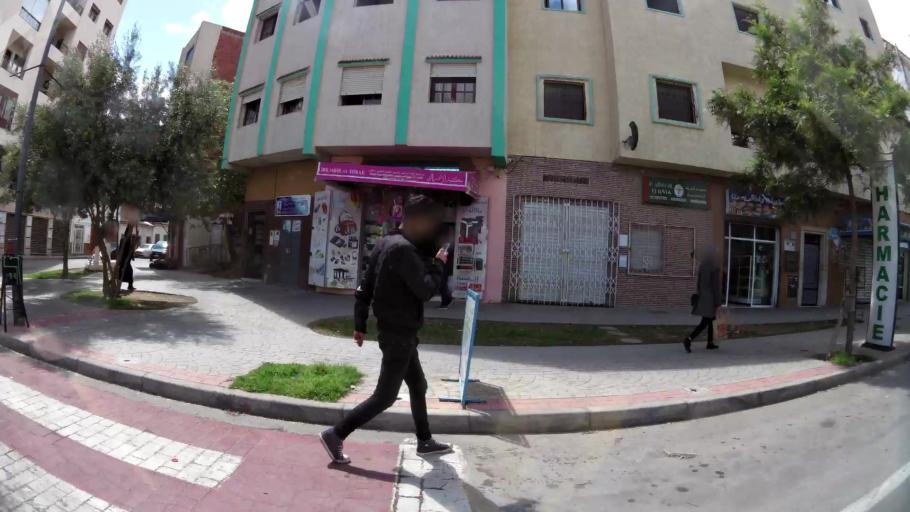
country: MA
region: Tanger-Tetouan
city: Tetouan
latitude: 35.5755
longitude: -5.3496
